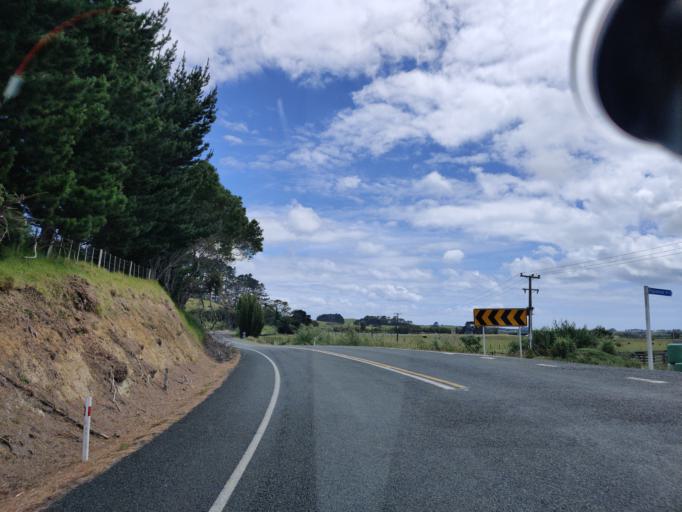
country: NZ
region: Northland
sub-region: Far North District
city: Kaitaia
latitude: -34.9800
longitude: 173.1933
